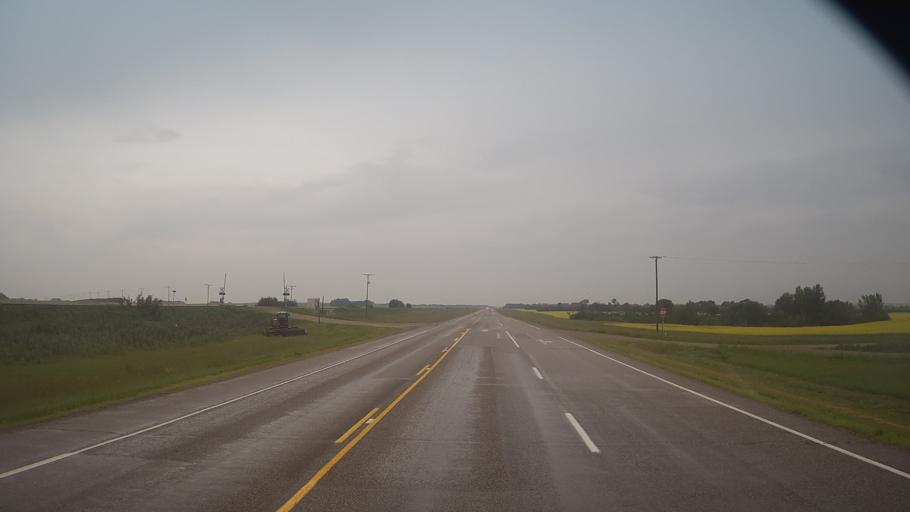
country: CA
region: Saskatchewan
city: Wilkie
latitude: 52.2304
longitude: -108.5398
